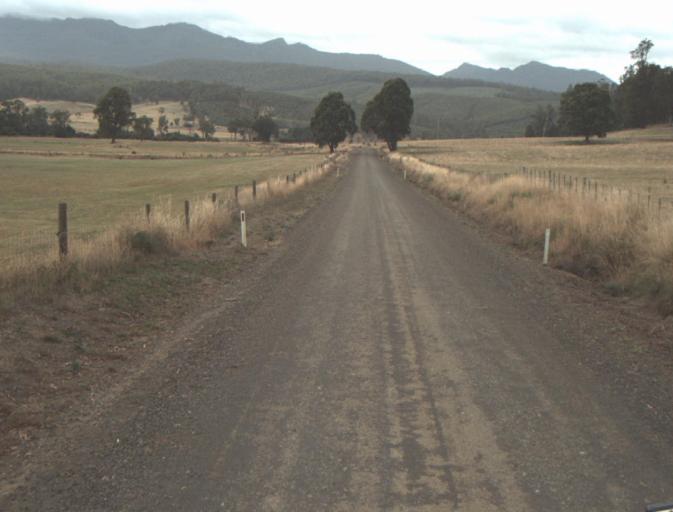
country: AU
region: Tasmania
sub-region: Northern Midlands
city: Evandale
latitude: -41.4604
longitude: 147.5333
